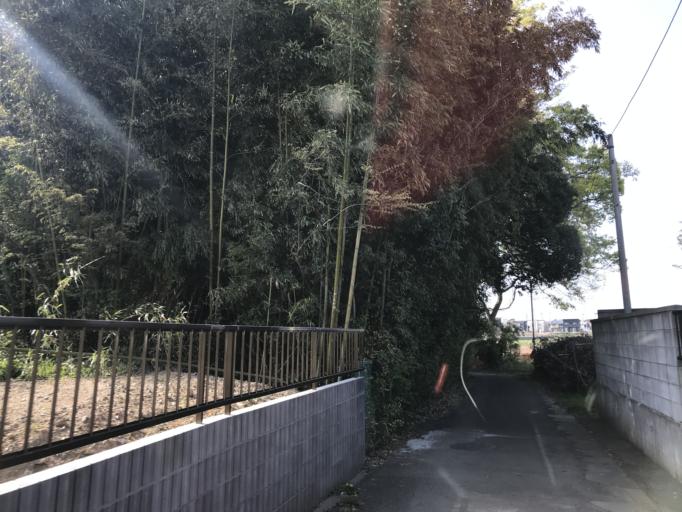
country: JP
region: Ibaraki
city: Mitsukaido
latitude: 35.9765
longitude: 139.9704
